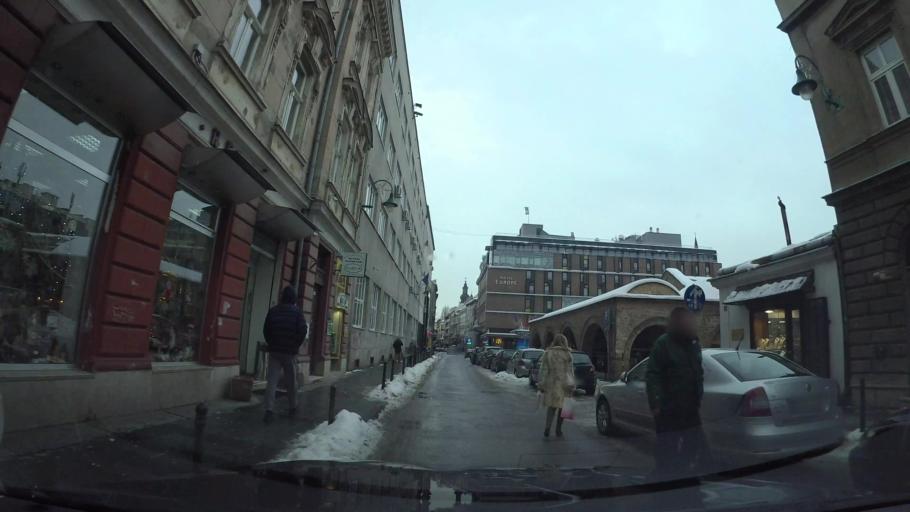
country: BA
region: Federation of Bosnia and Herzegovina
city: Kobilja Glava
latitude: 43.8583
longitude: 18.4284
